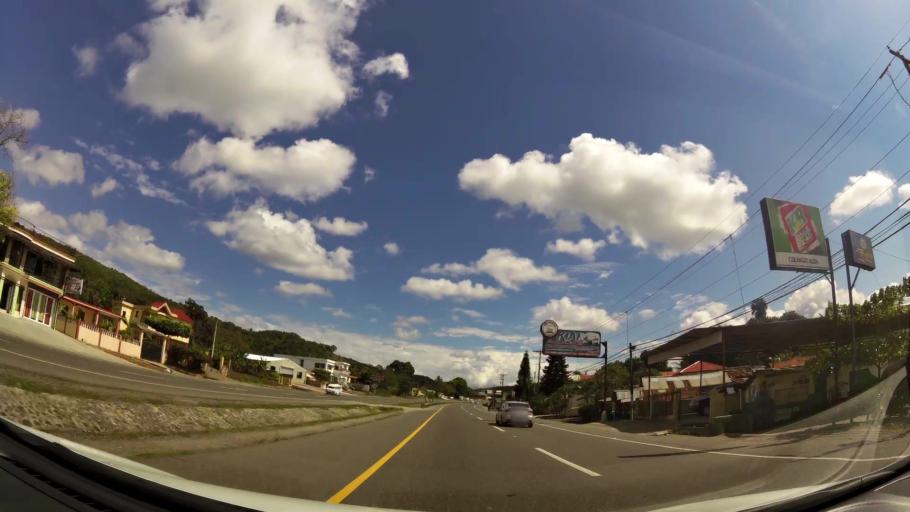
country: DO
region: La Vega
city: Rio Verde Arriba
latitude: 19.2988
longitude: -70.5806
